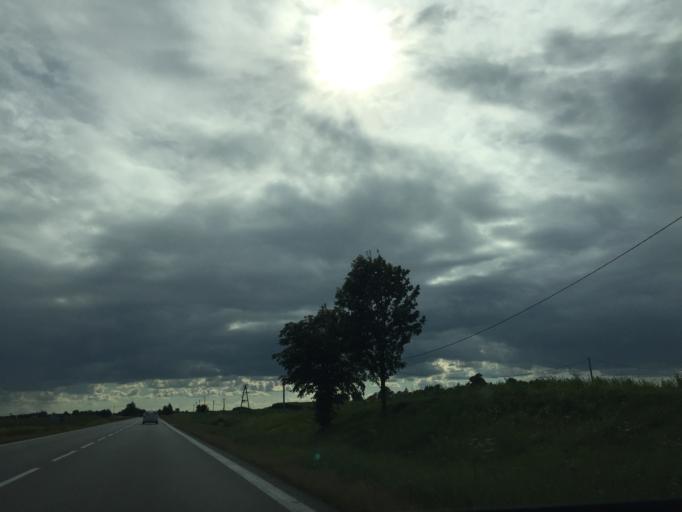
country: PL
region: Podlasie
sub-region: Powiat augustowski
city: Augustow
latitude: 53.8137
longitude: 22.9188
